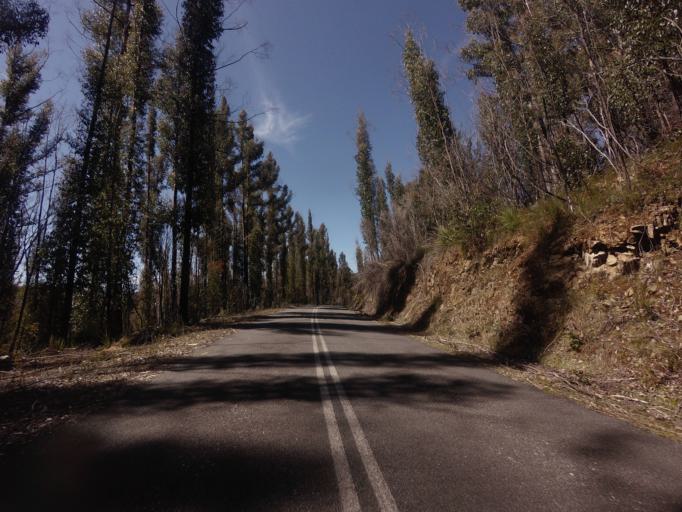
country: AU
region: Tasmania
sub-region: Huon Valley
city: Geeveston
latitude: -42.8410
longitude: 146.2543
